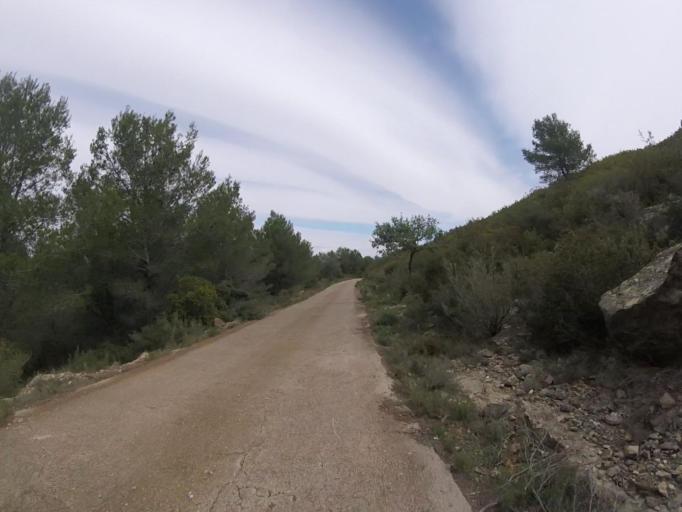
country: ES
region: Valencia
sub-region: Provincia de Castello
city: Cabanes
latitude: 40.1907
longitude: 0.0787
